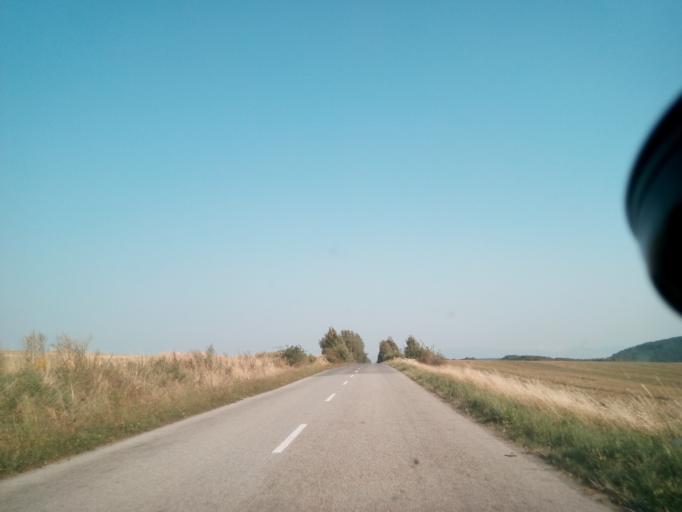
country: SK
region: Kosicky
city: Kosice
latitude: 48.7288
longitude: 21.1156
